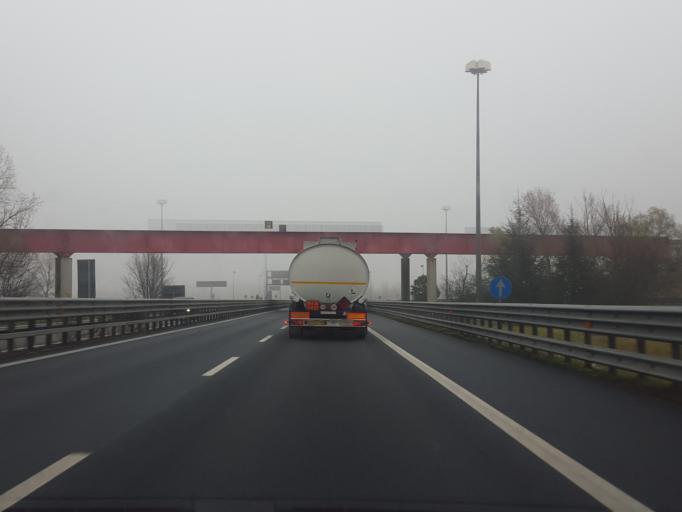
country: IT
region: Veneto
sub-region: Provincia di Venezia
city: Dese
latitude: 45.5358
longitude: 12.2801
